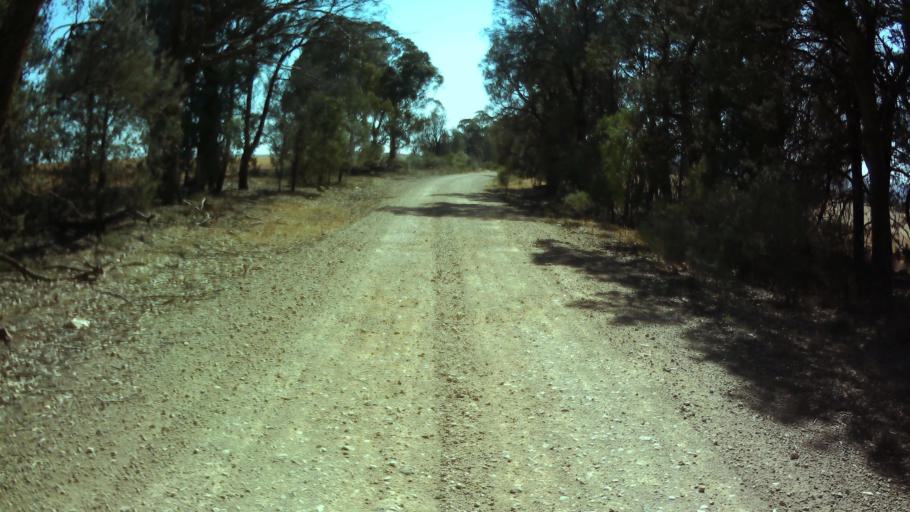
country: AU
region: New South Wales
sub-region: Weddin
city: Grenfell
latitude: -33.9046
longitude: 147.8583
